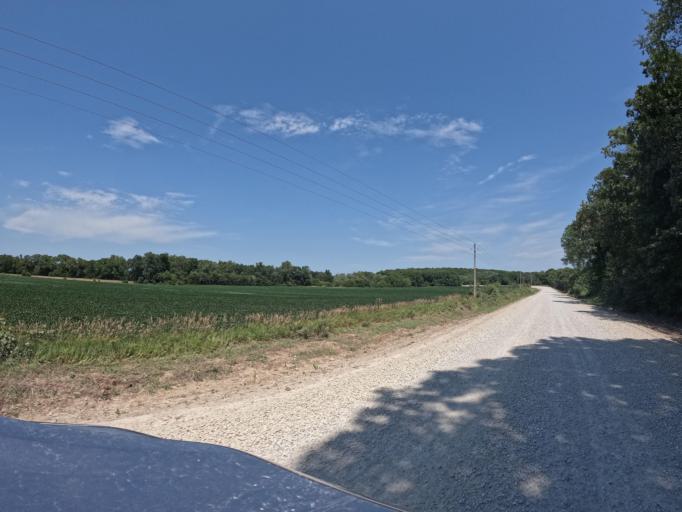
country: US
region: Iowa
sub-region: Henry County
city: Mount Pleasant
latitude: 40.9047
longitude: -91.6756
